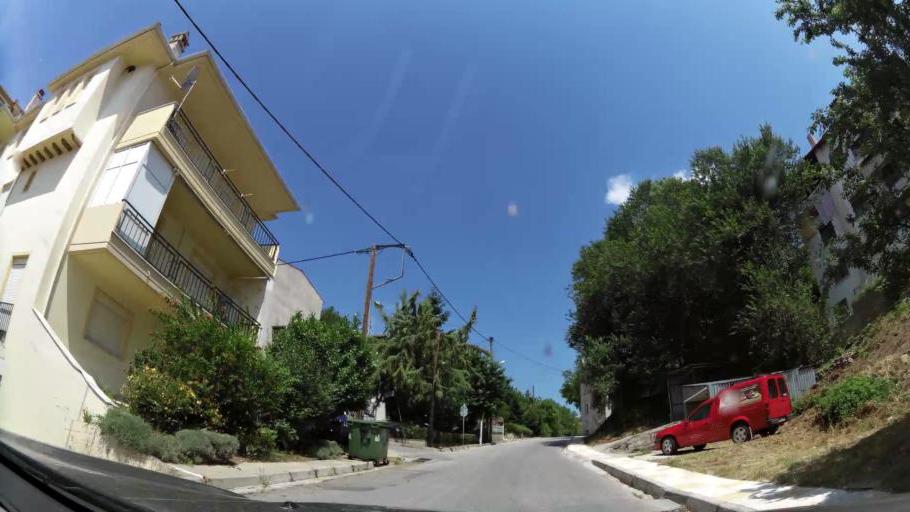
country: GR
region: West Macedonia
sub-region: Nomos Kozanis
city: Kozani
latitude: 40.3009
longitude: 21.7806
